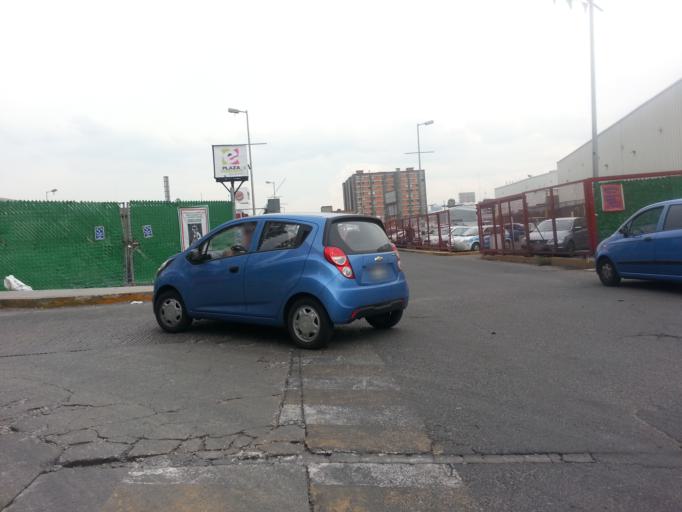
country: MX
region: Mexico City
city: Colonia del Valle
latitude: 19.3869
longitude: -99.1914
